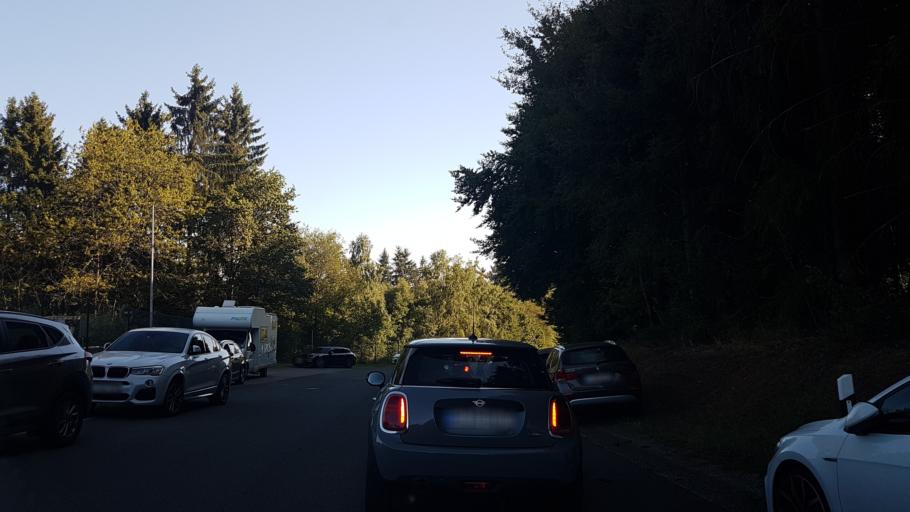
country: DE
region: Rheinland-Pfalz
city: Baumholder
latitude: 49.6303
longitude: 7.3151
